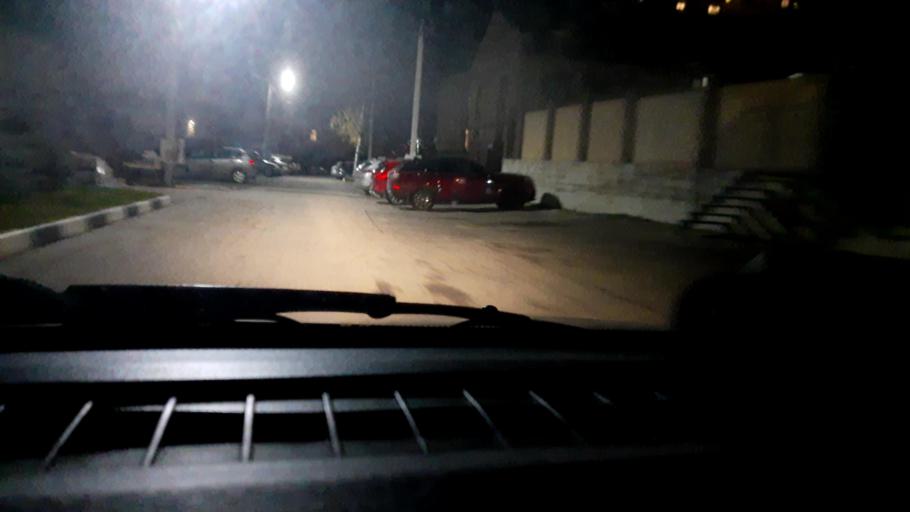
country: RU
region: Nizjnij Novgorod
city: Afonino
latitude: 56.2818
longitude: 44.0624
